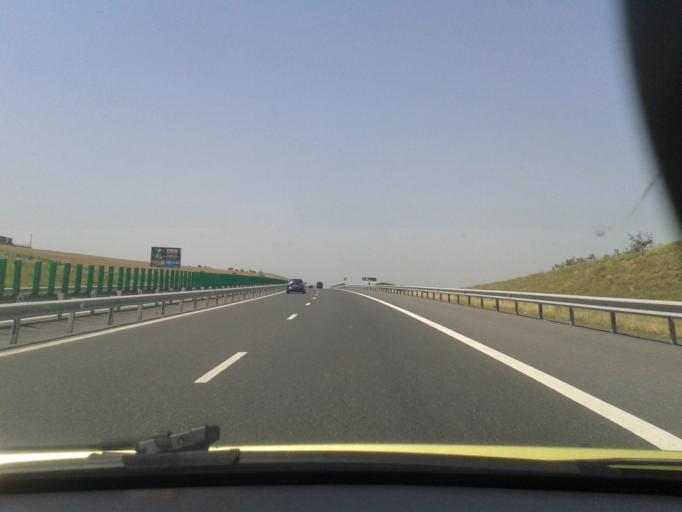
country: RO
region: Constanta
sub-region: Oras Cernavoda
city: Cernavoda
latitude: 44.3116
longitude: 28.0373
